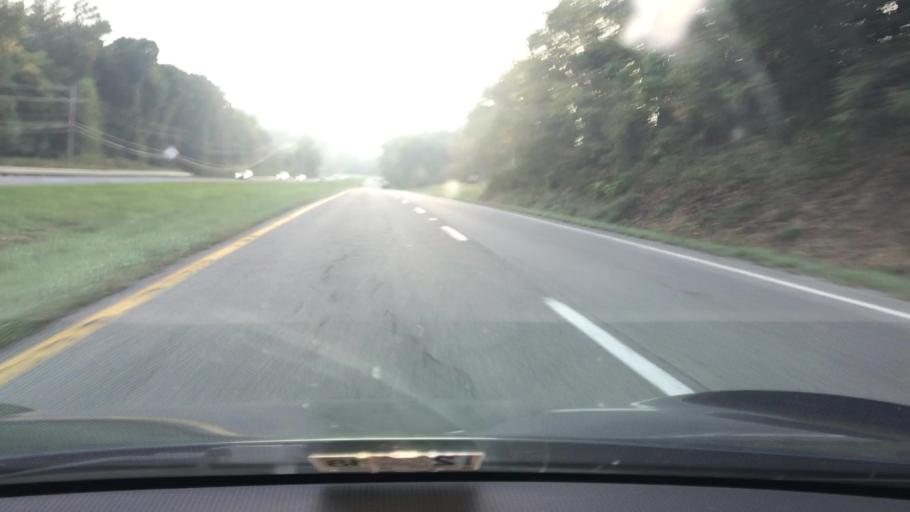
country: US
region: Virginia
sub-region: Botetourt County
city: Blue Ridge
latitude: 37.3972
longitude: -79.7603
